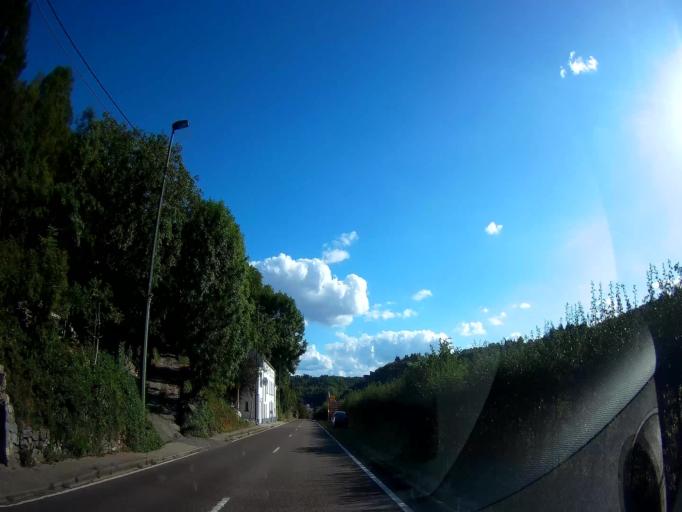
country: BE
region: Wallonia
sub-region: Province de Namur
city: Dinant
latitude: 50.2813
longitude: 4.8967
